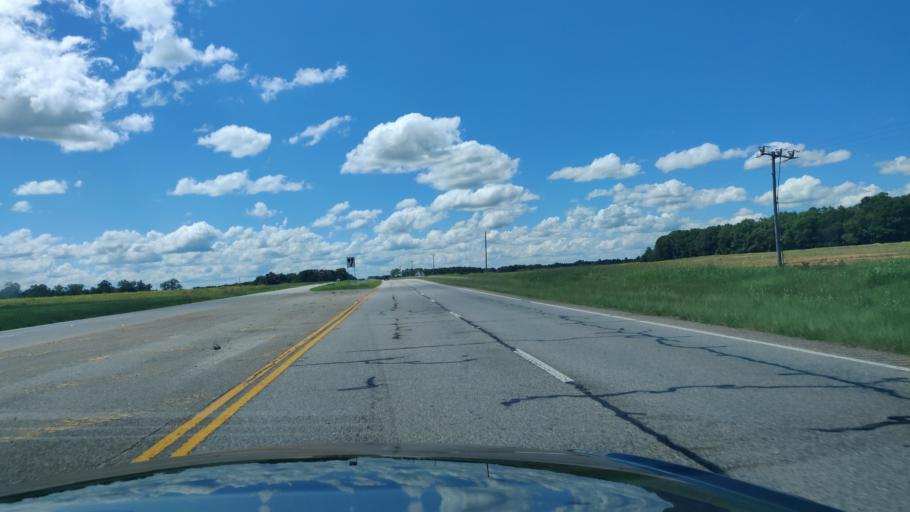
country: US
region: Georgia
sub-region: Stewart County
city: Richland
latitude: 31.9860
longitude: -84.6279
